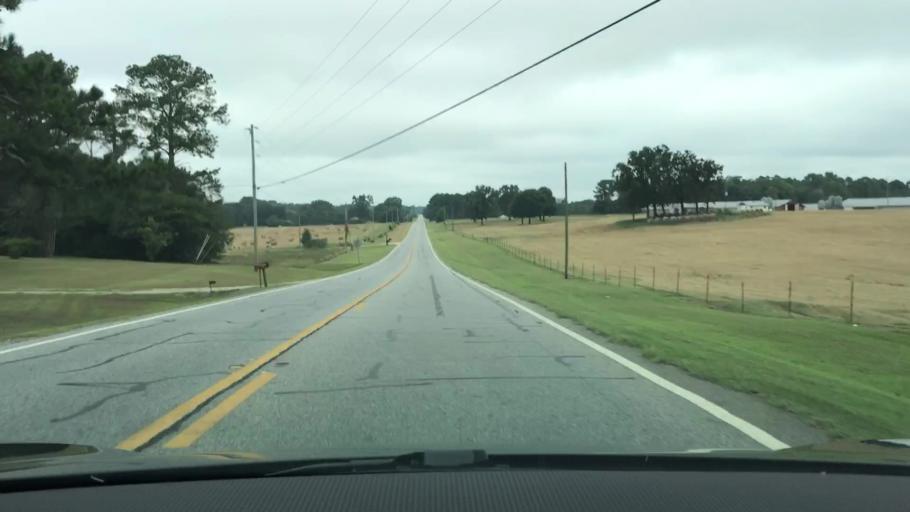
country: US
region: Georgia
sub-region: Oconee County
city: Watkinsville
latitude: 33.7917
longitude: -83.3234
